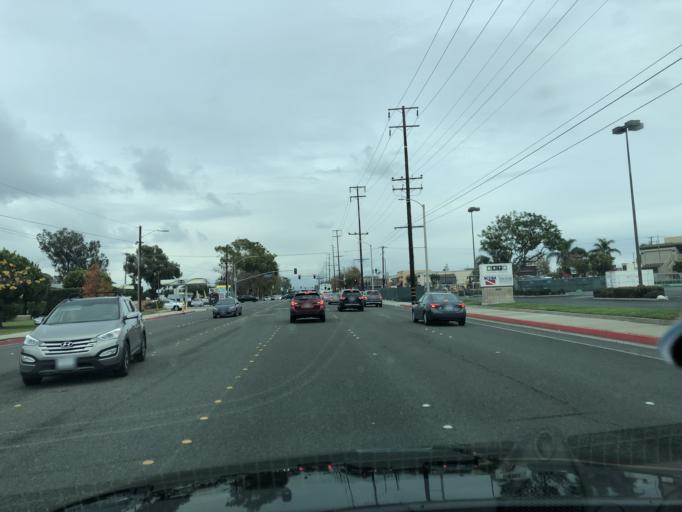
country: US
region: California
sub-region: Orange County
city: Midway City
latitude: 33.7301
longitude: -118.0085
